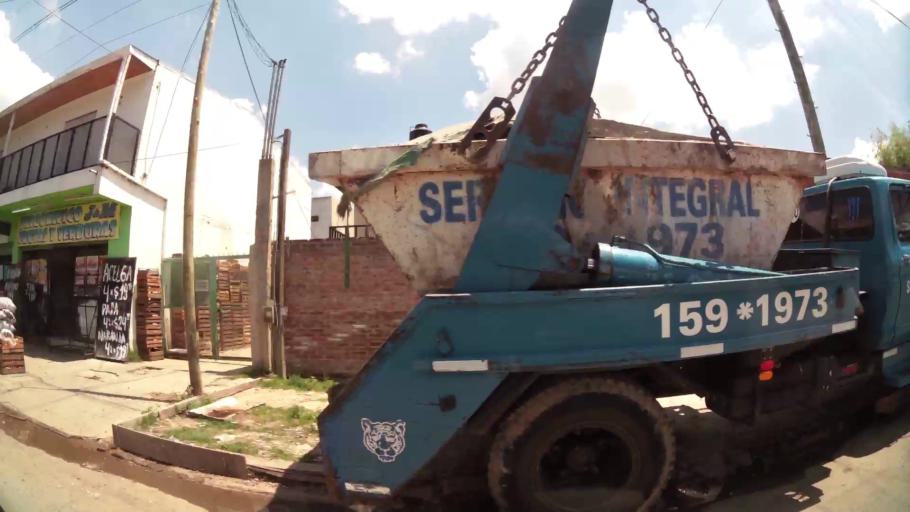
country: AR
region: Buenos Aires
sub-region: Partido de Tigre
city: Tigre
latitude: -34.4091
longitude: -58.6041
